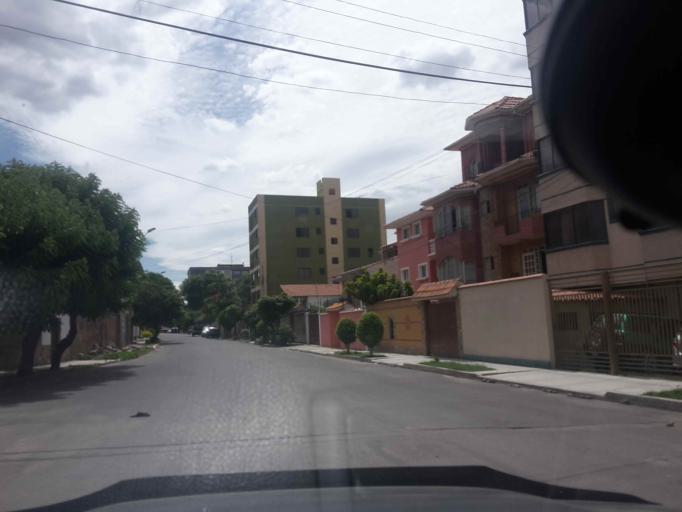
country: BO
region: Cochabamba
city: Cochabamba
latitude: -17.3629
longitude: -66.1733
